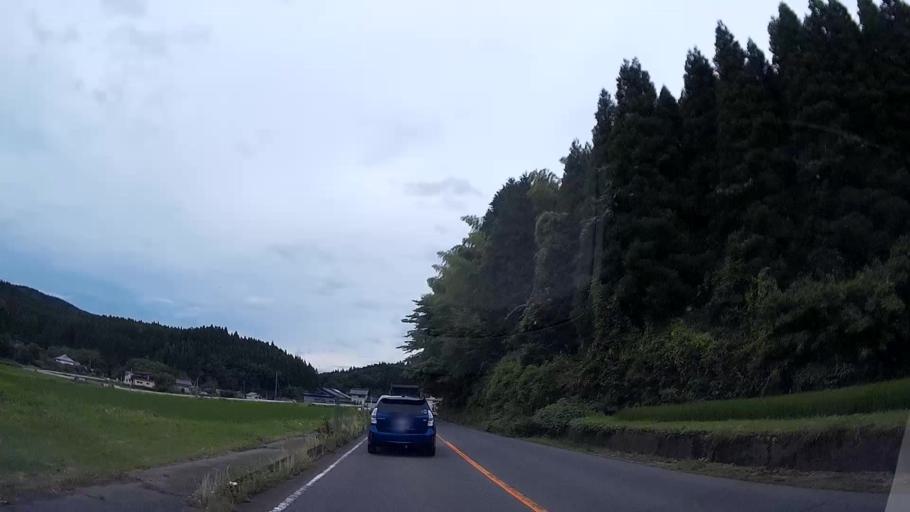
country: JP
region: Oita
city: Tsukawaki
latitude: 33.1264
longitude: 131.0331
